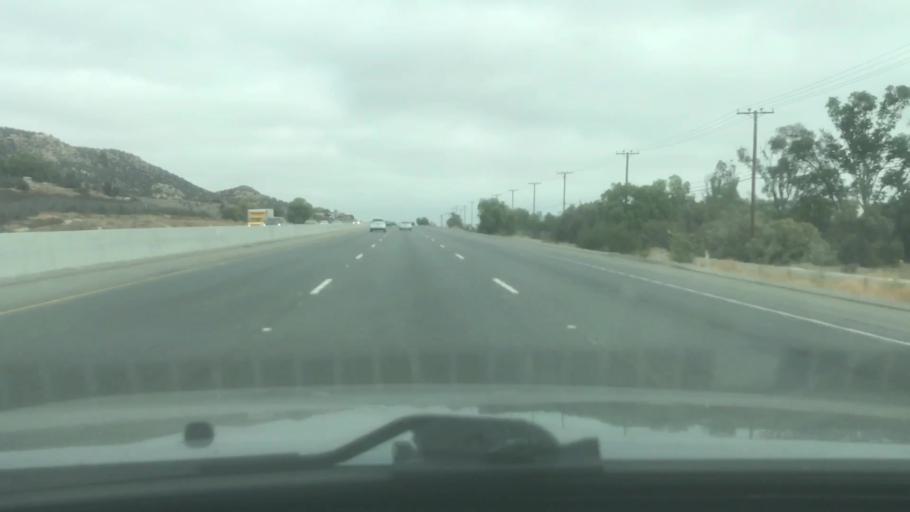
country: US
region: California
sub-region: Riverside County
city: Murrieta Hot Springs
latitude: 33.6068
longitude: -117.1705
